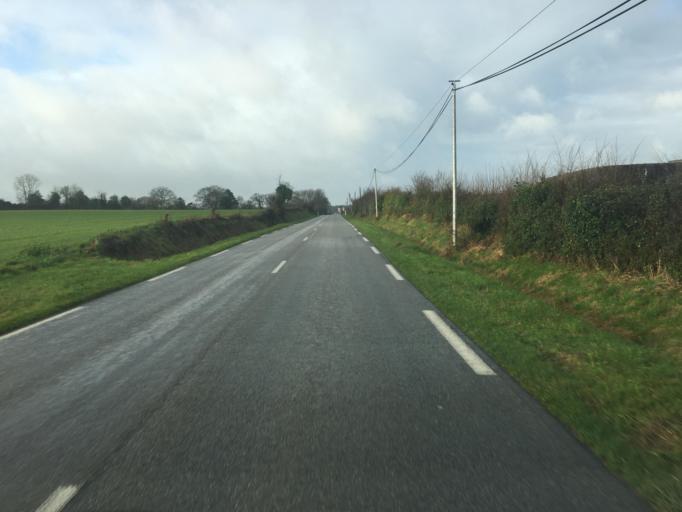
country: FR
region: Lower Normandy
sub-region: Departement de la Manche
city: Saint-Pierre-Eglise
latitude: 49.6678
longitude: -1.3842
